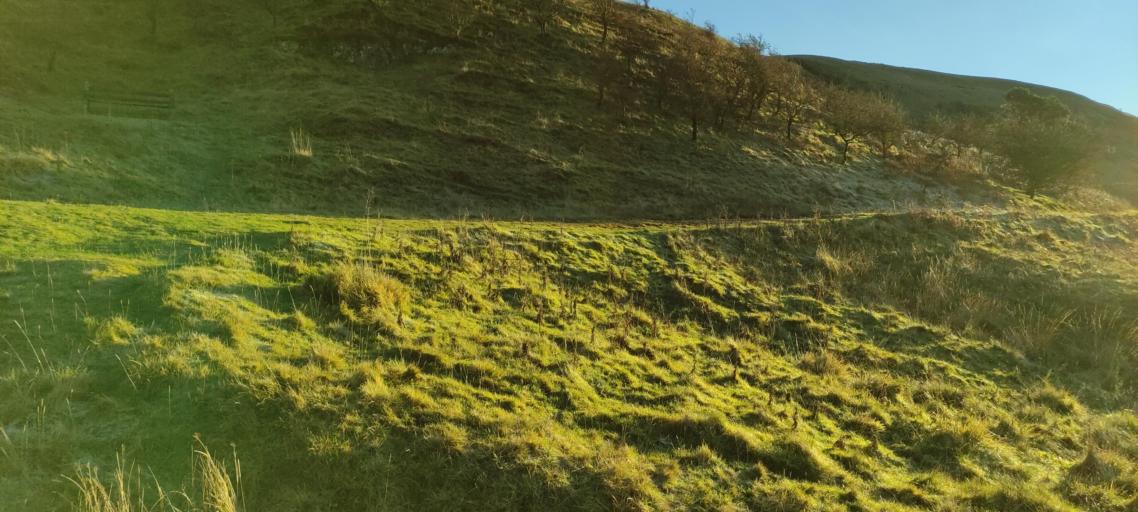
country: GB
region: Scotland
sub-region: Dumfries and Galloway
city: Langholm
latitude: 55.1525
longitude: -2.9854
